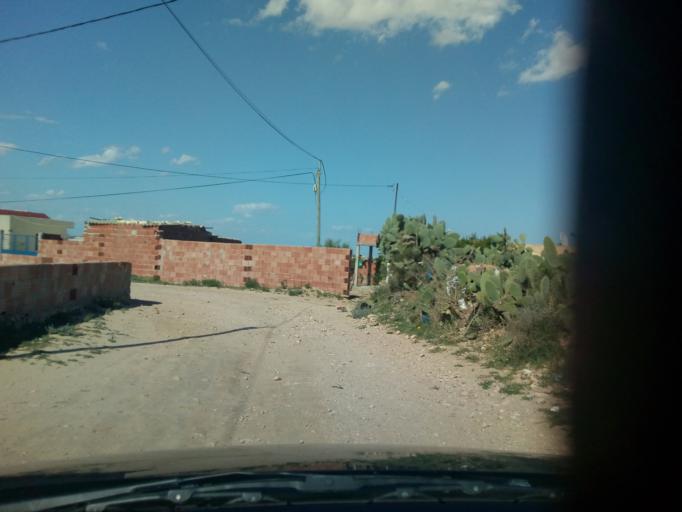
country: TN
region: Safaqis
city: Sfax
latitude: 34.7279
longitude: 10.6009
